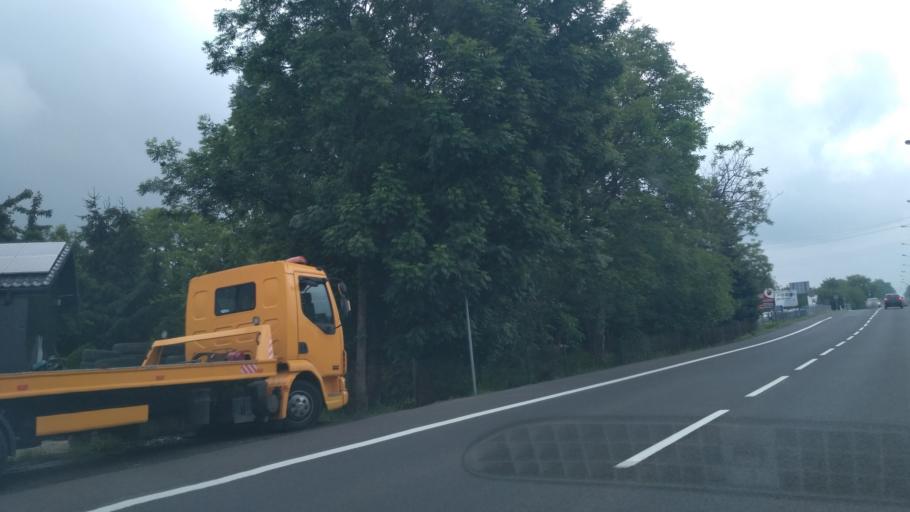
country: PL
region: Subcarpathian Voivodeship
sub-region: Powiat przeworski
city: Przeworsk
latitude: 50.0569
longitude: 22.5034
